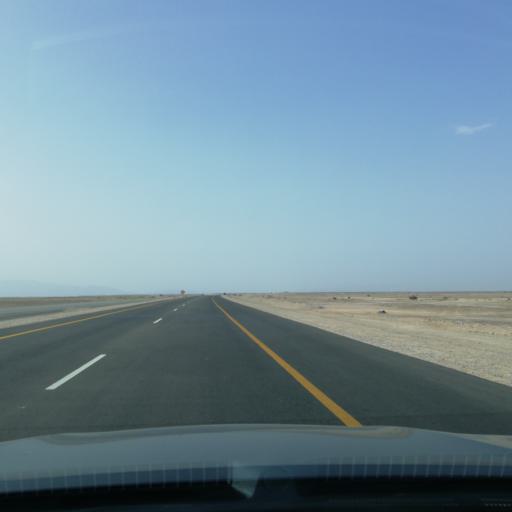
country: OM
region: Muhafazat ad Dakhiliyah
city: Adam
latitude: 22.1520
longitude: 57.5214
